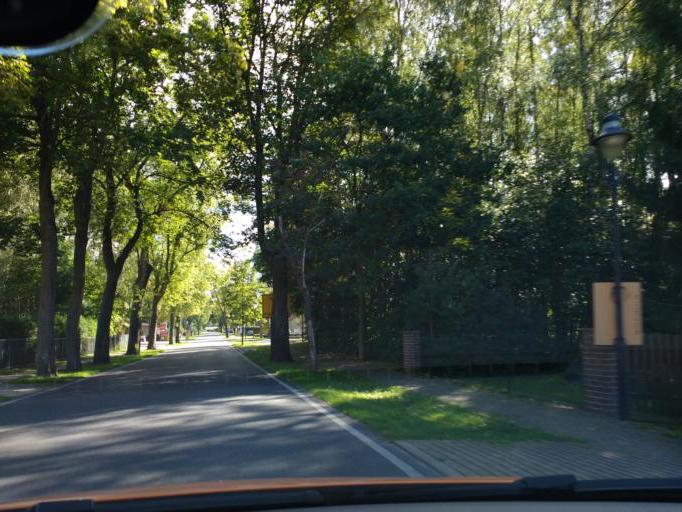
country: DE
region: Brandenburg
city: Munchehofe
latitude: 52.2247
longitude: 13.7695
